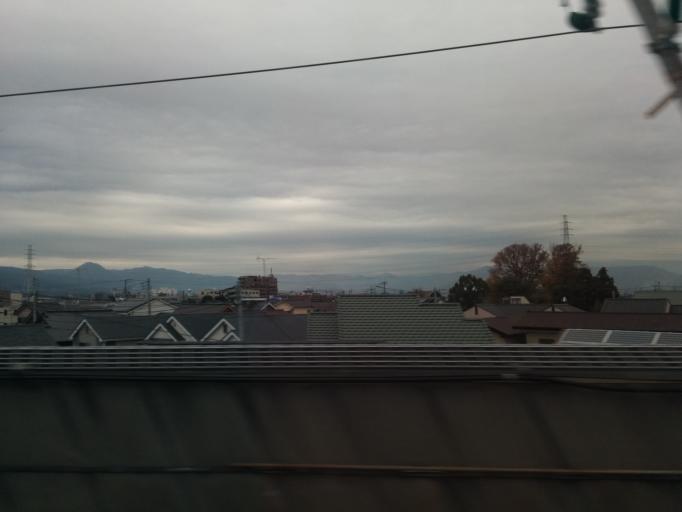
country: JP
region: Kanagawa
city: Odawara
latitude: 35.2780
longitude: 139.1780
